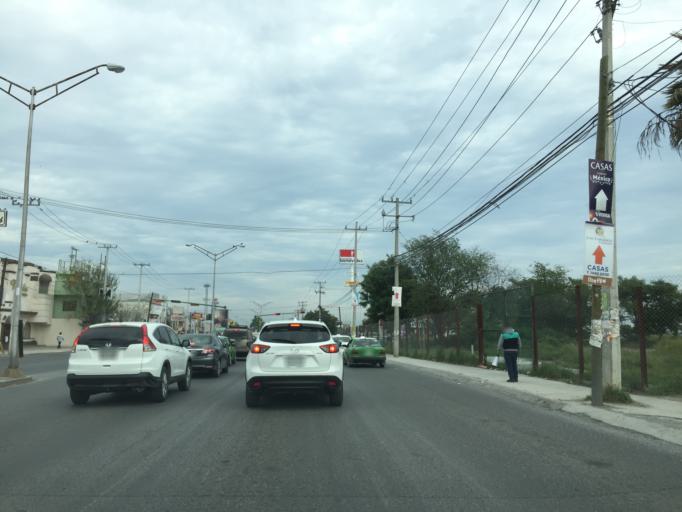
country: MX
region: Nuevo Leon
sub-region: Juarez
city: Valle de Juarez
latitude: 25.6601
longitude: -100.1792
